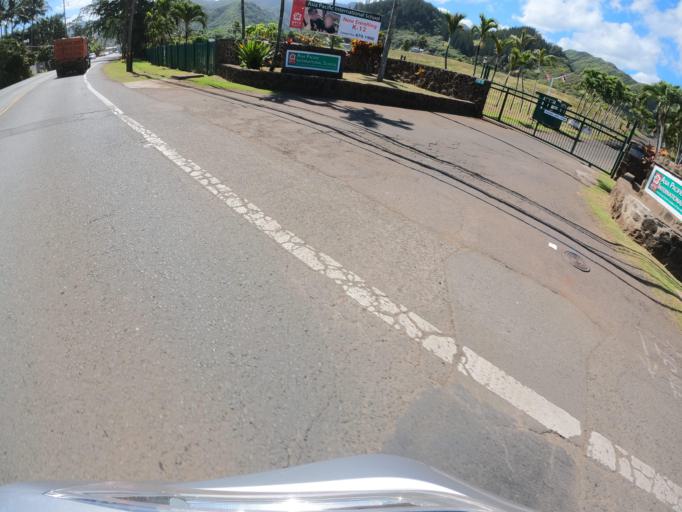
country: US
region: Hawaii
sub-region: Honolulu County
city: Hau'ula
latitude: 21.6166
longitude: -157.9136
